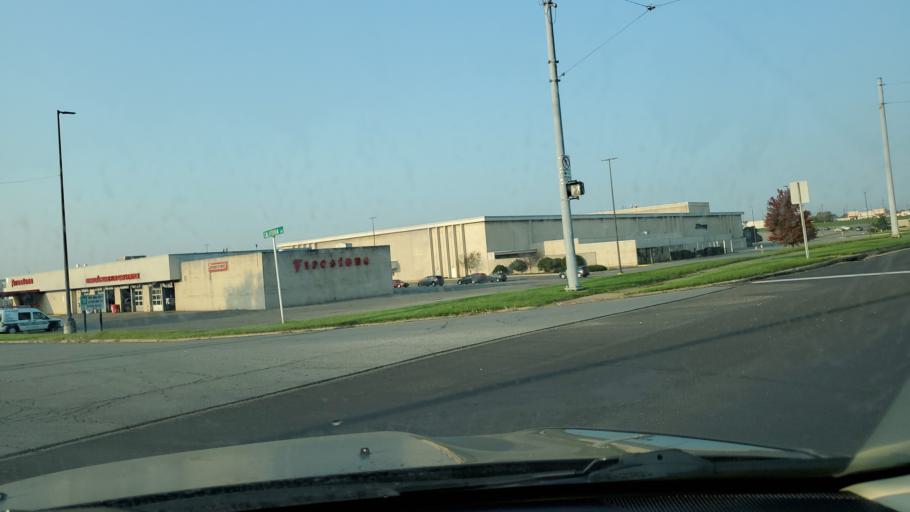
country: US
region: Ohio
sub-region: Mahoning County
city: Boardman
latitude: 41.0244
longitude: -80.6564
